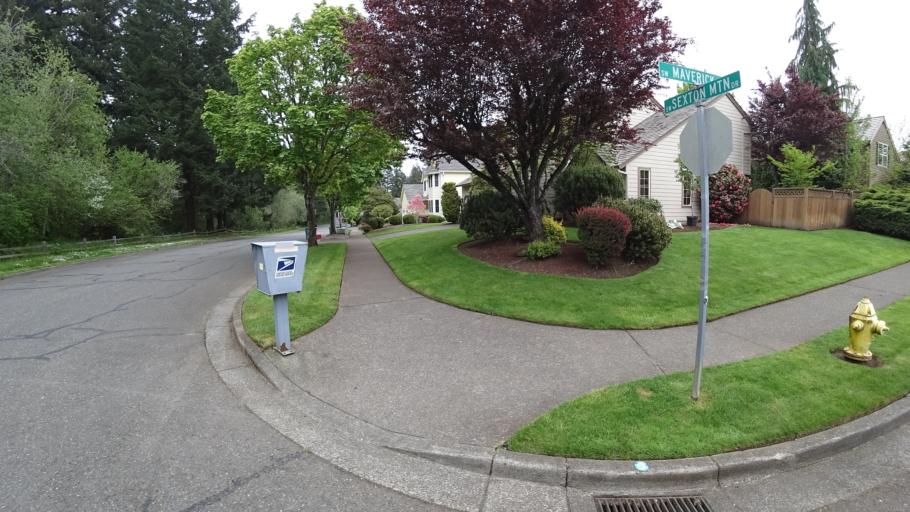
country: US
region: Oregon
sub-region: Washington County
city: Beaverton
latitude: 45.4602
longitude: -122.8226
